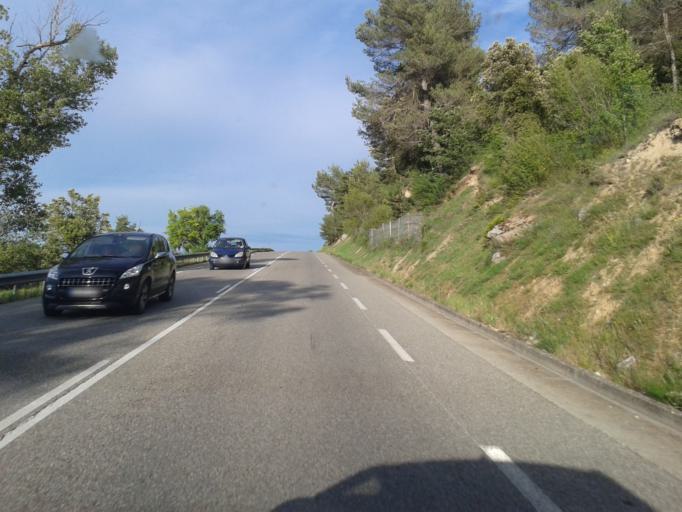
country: FR
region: Provence-Alpes-Cote d'Azur
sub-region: Departement du Vaucluse
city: Beaumont-de-Pertuis
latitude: 43.6891
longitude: 5.6865
